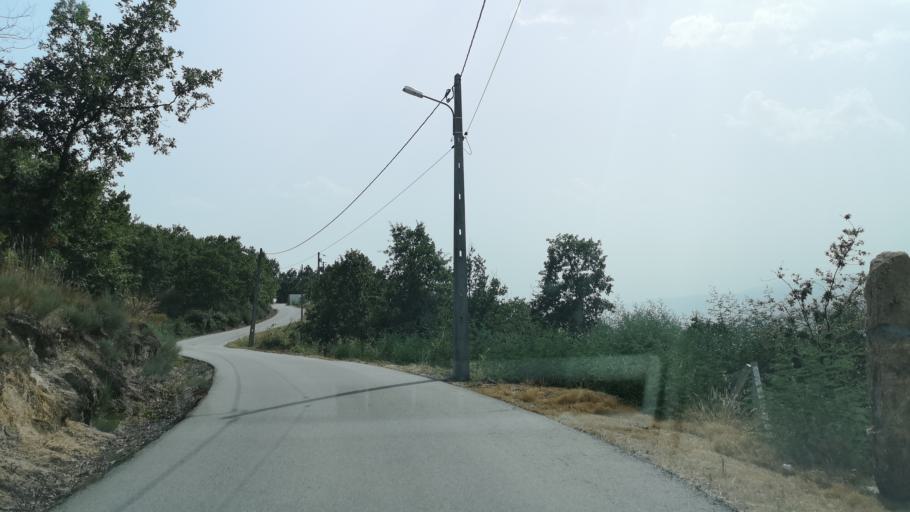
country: PT
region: Castelo Branco
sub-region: Belmonte
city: Belmonte
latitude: 40.3469
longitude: -7.3583
